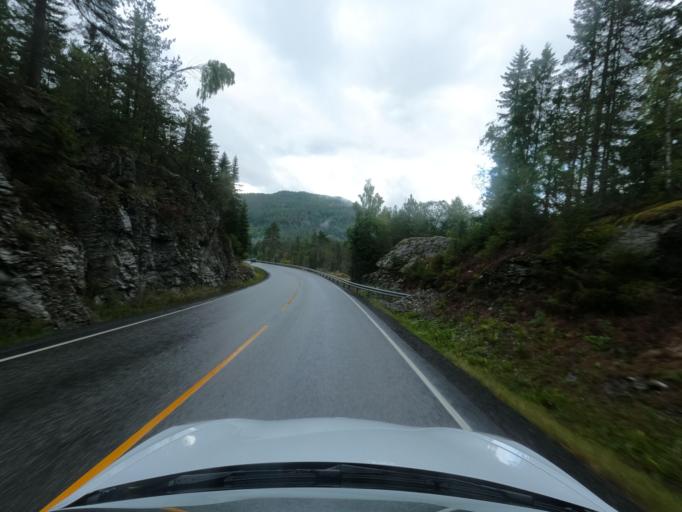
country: NO
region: Telemark
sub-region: Kviteseid
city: Kviteseid
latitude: 59.4459
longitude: 8.5596
